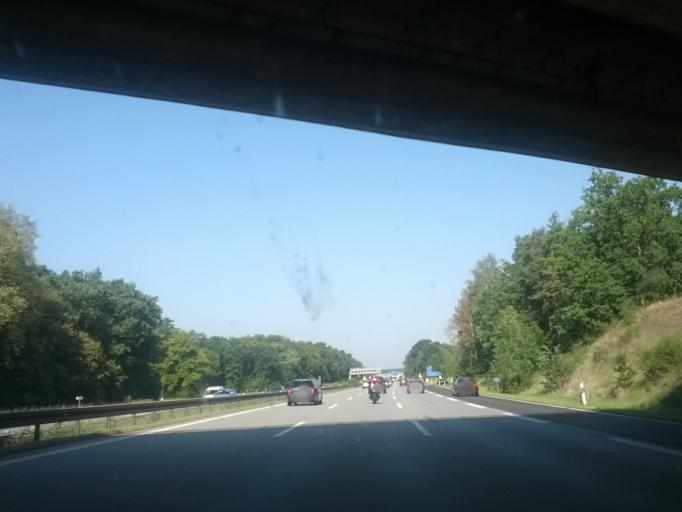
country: DE
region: Brandenburg
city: Wildau
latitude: 52.3125
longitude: 13.6033
